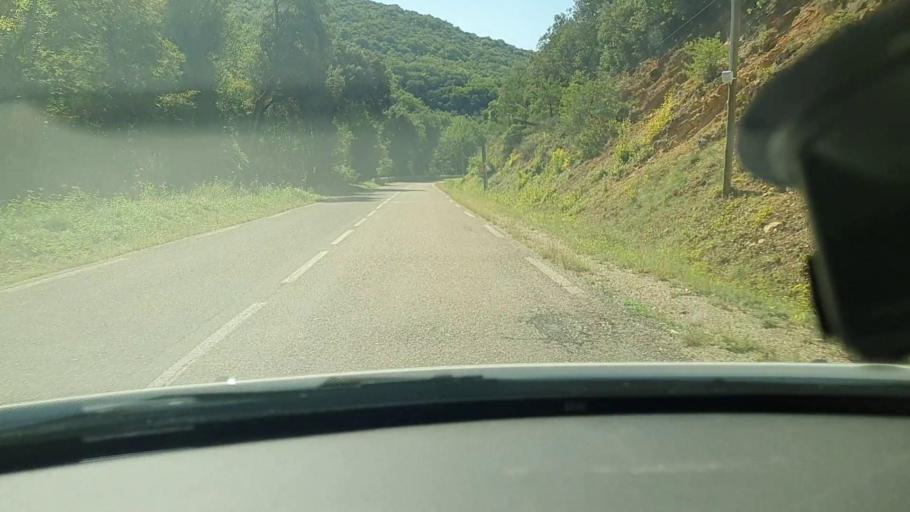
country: FR
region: Languedoc-Roussillon
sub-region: Departement du Gard
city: Saint-Paulet-de-Caisson
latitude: 44.2217
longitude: 4.5431
